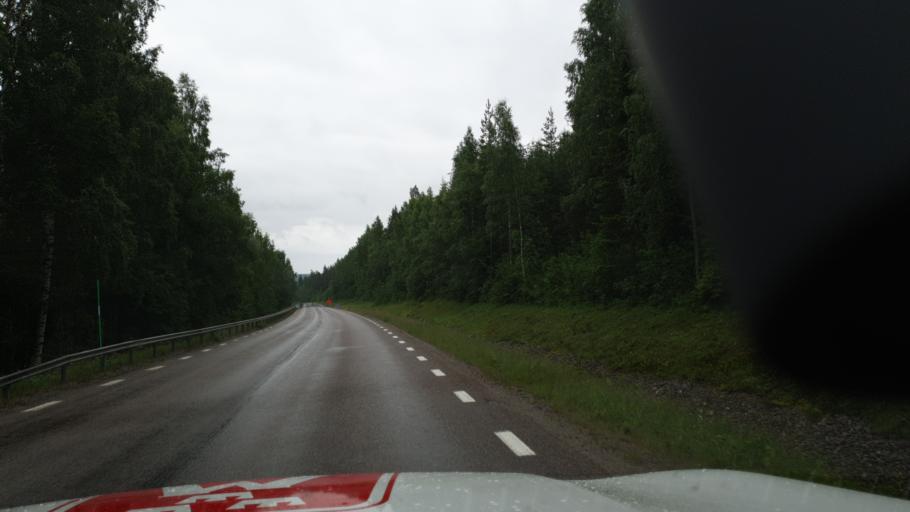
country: SE
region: Vaesterbotten
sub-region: Vannas Kommun
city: Vaennaes
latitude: 63.7887
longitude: 19.8260
